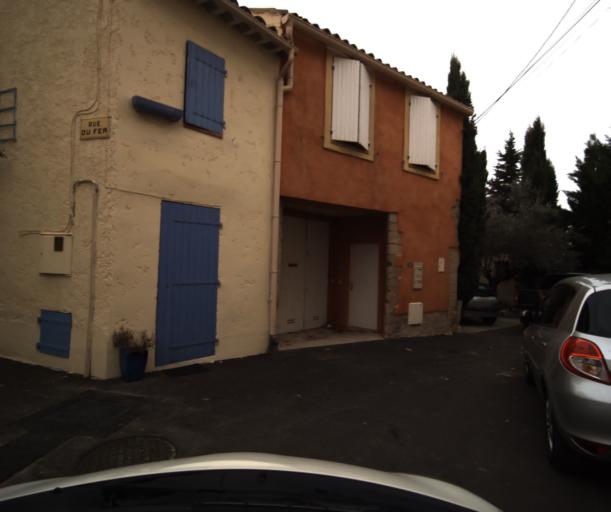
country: FR
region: Provence-Alpes-Cote d'Azur
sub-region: Departement du Vaucluse
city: Pertuis
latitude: 43.6962
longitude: 5.5022
